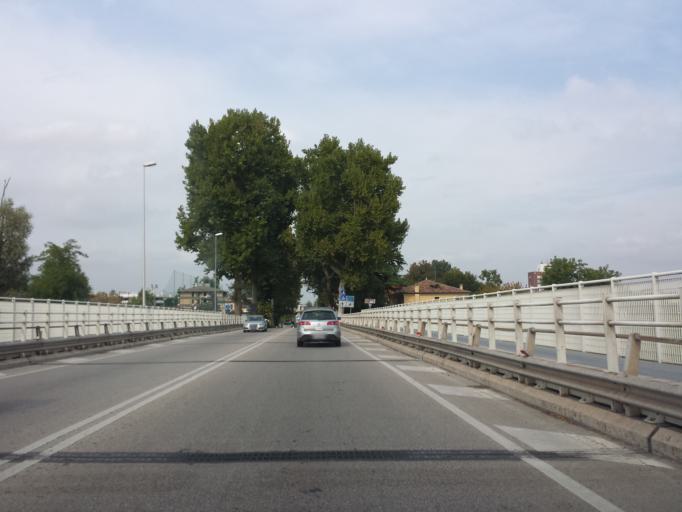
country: IT
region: Veneto
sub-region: Provincia di Padova
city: Vigodarzere
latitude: 45.4465
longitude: 11.8938
